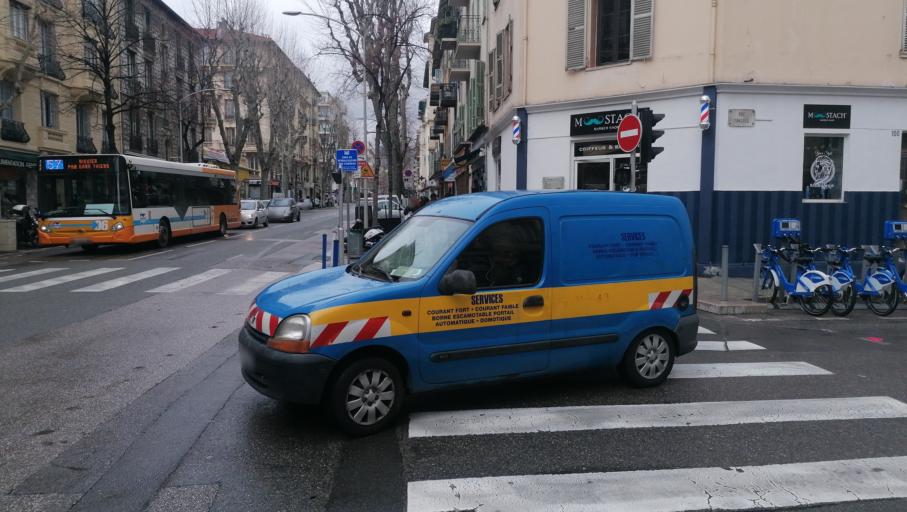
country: FR
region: Provence-Alpes-Cote d'Azur
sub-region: Departement des Alpes-Maritimes
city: Nice
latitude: 43.7057
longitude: 7.2561
